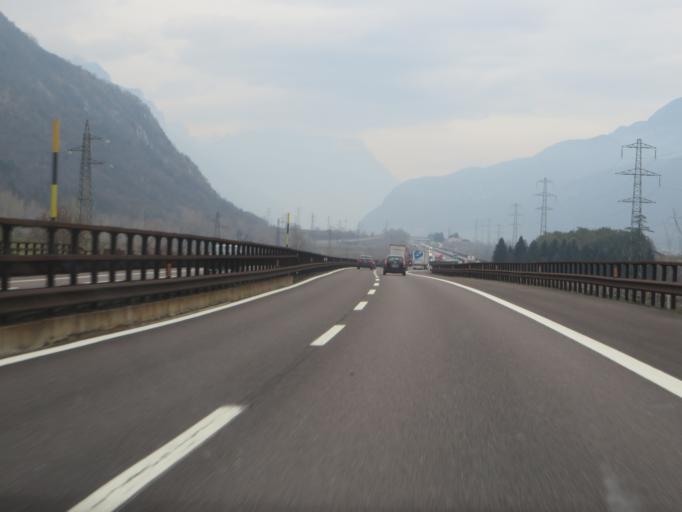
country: IT
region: Veneto
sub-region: Provincia di Verona
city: Rivalta
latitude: 45.6399
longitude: 10.8784
